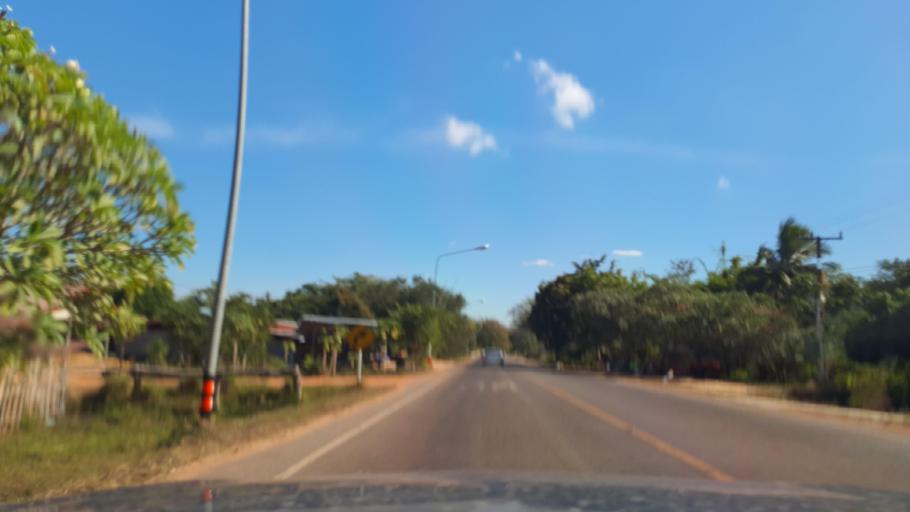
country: TH
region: Kalasin
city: Khao Wong
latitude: 16.7846
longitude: 104.1485
